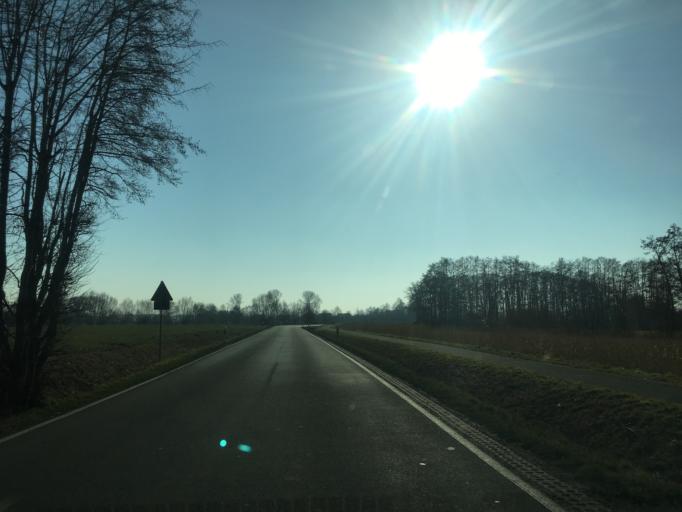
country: DE
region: North Rhine-Westphalia
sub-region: Regierungsbezirk Munster
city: Altenberge
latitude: 52.0237
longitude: 7.4459
